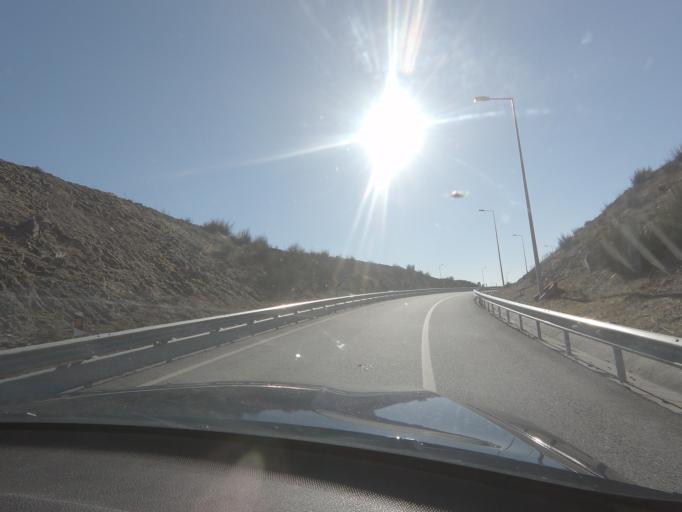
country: PT
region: Viseu
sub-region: Viseu
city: Abraveses
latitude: 40.6771
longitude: -7.9687
